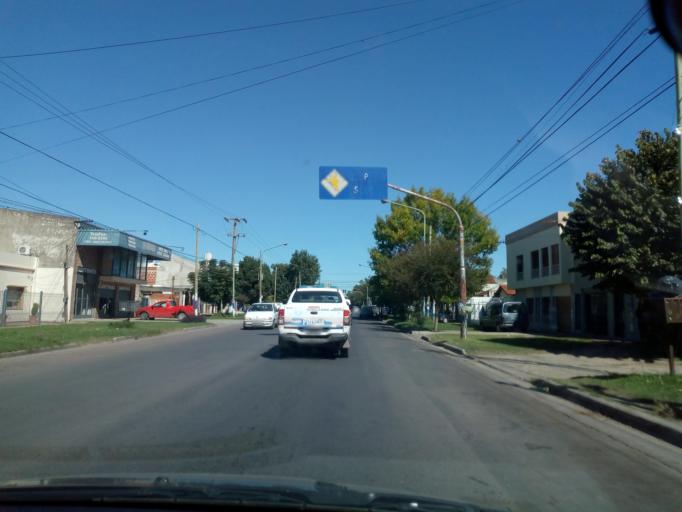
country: AR
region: Buenos Aires
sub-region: Partido de La Plata
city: La Plata
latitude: -34.9649
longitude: -57.9775
